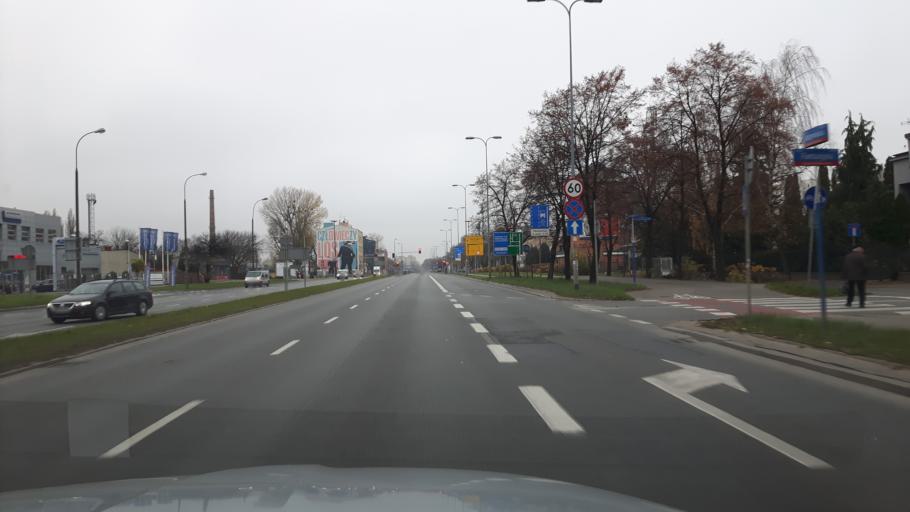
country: PL
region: Masovian Voivodeship
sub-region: Warszawa
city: Targowek
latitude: 52.2746
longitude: 21.0652
